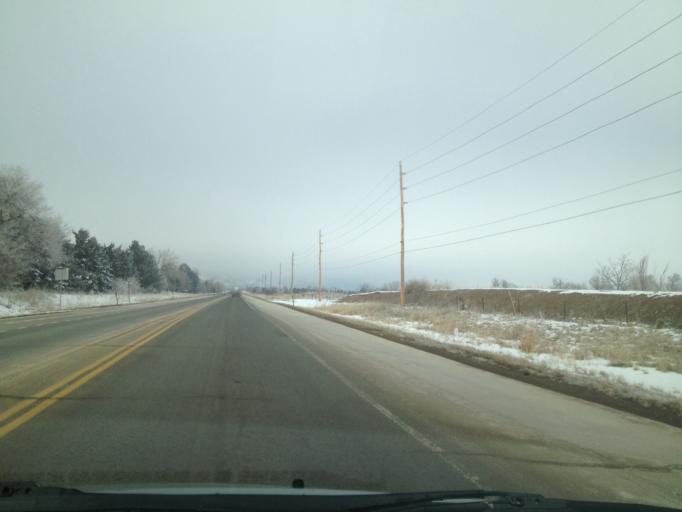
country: US
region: Colorado
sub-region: Boulder County
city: Boulder
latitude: 40.0557
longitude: -105.2667
